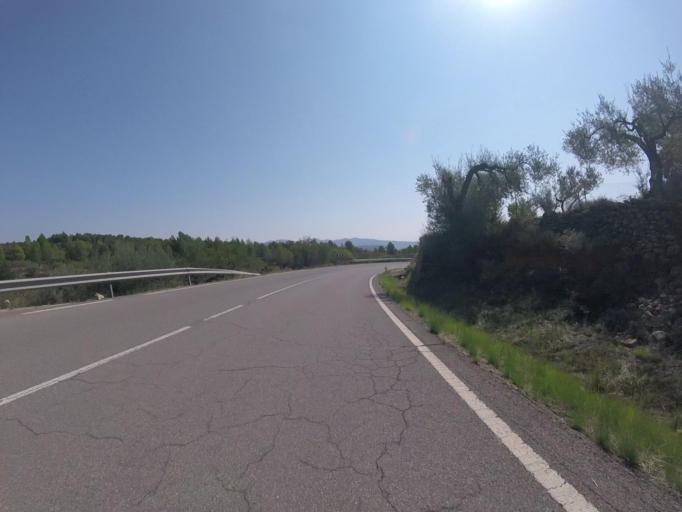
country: ES
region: Valencia
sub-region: Provincia de Castello
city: Adzaneta
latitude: 40.2376
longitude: -0.1849
